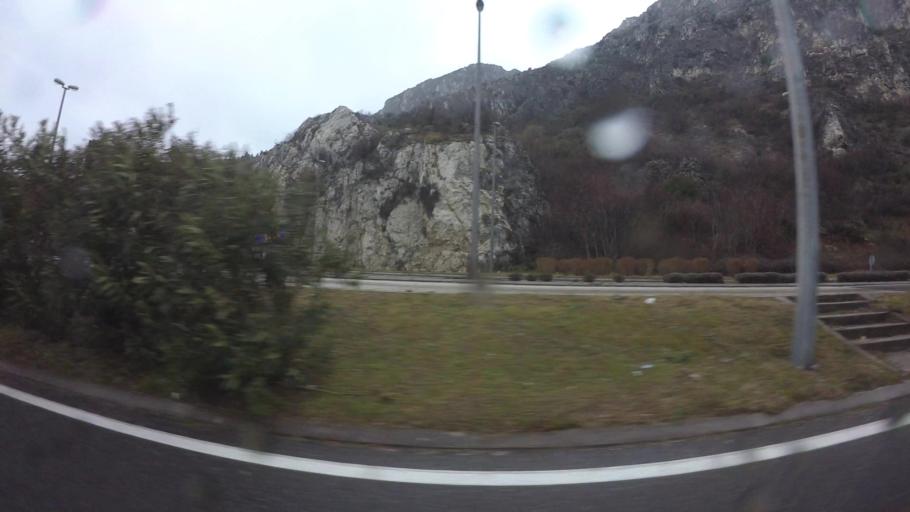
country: BA
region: Federation of Bosnia and Herzegovina
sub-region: Hercegovacko-Bosanski Kanton
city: Mostar
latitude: 43.3273
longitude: 17.8165
